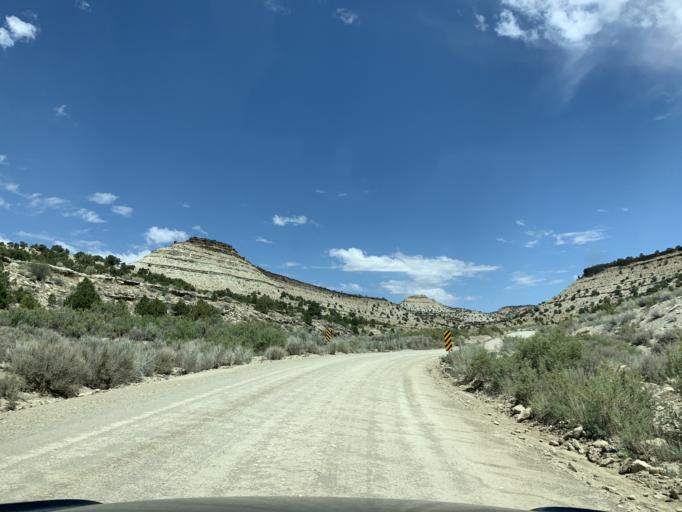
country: US
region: Utah
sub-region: Carbon County
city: East Carbon City
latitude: 39.8491
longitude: -110.2539
